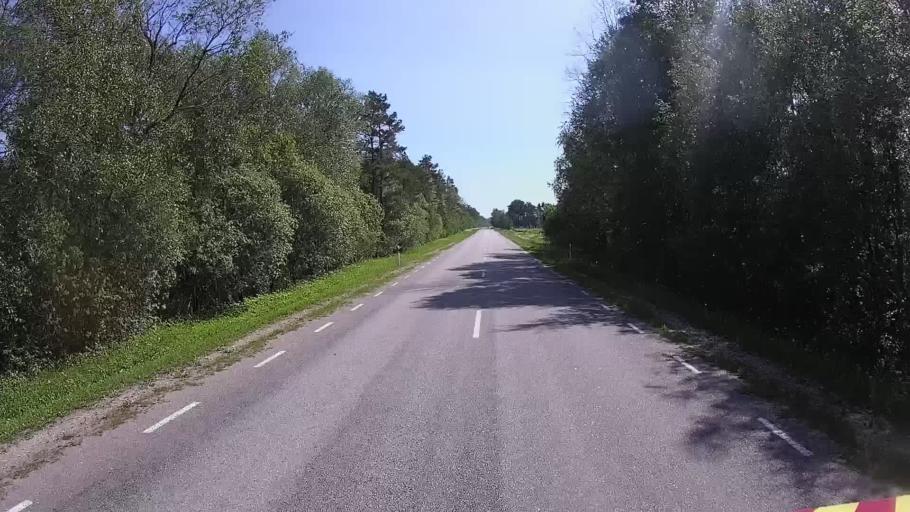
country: EE
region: Saare
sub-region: Kuressaare linn
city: Kuressaare
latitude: 58.4037
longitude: 22.4276
